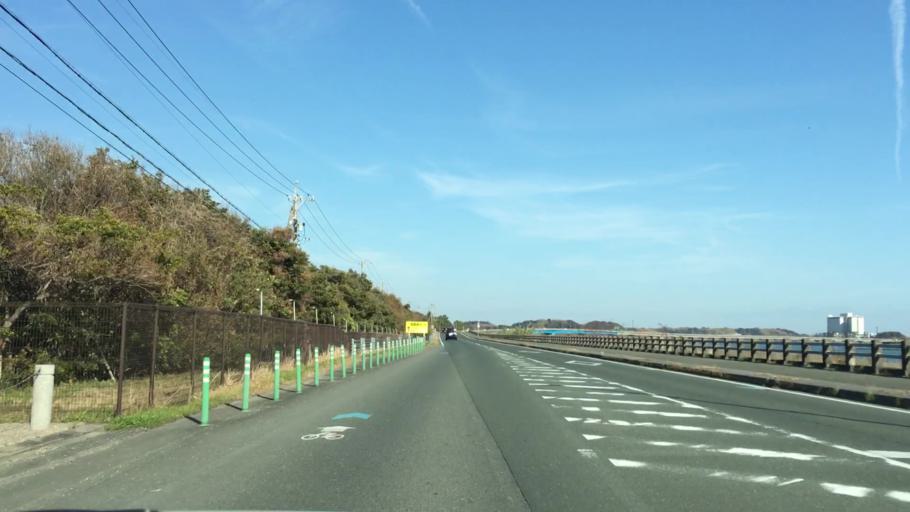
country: JP
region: Shizuoka
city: Kosai-shi
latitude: 34.7121
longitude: 137.5953
